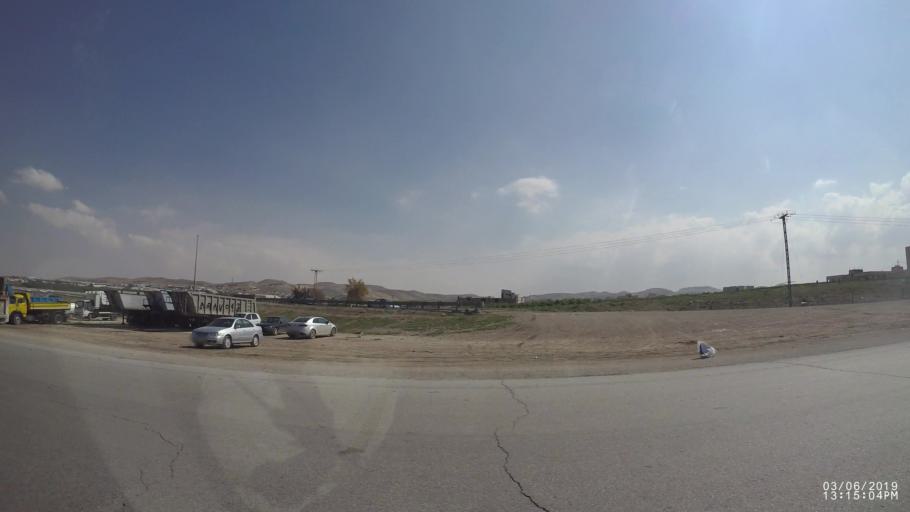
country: JO
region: Zarqa
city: Russeifa
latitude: 32.0187
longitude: 36.0754
